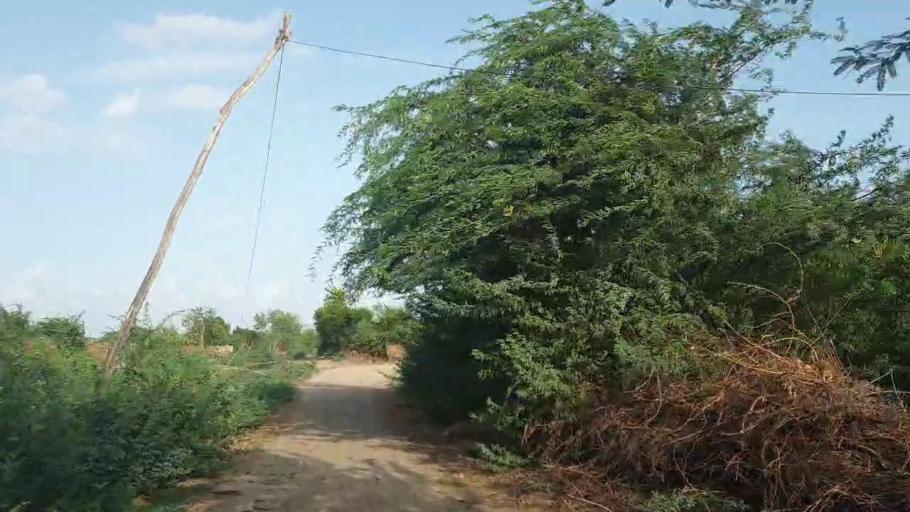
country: PK
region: Sindh
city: Kadhan
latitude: 24.6387
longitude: 69.1046
